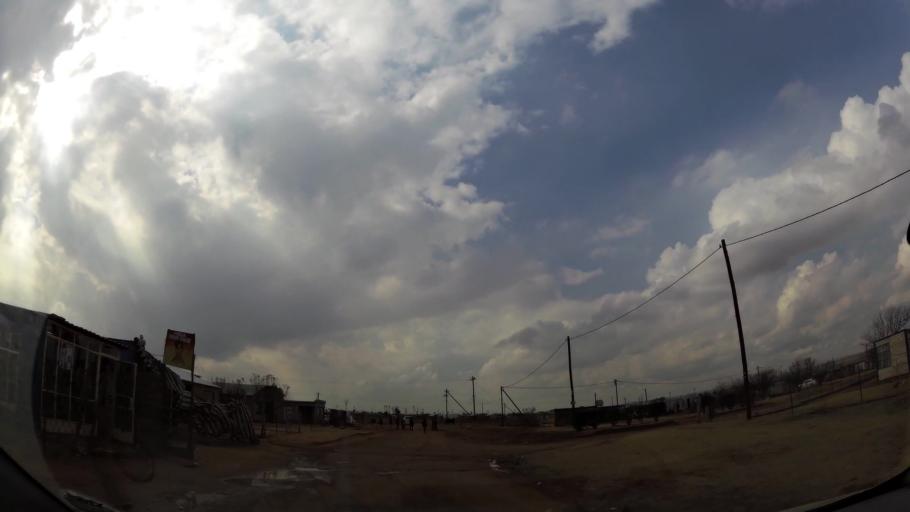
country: ZA
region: Orange Free State
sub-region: Fezile Dabi District Municipality
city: Sasolburg
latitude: -26.8606
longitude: 27.9028
